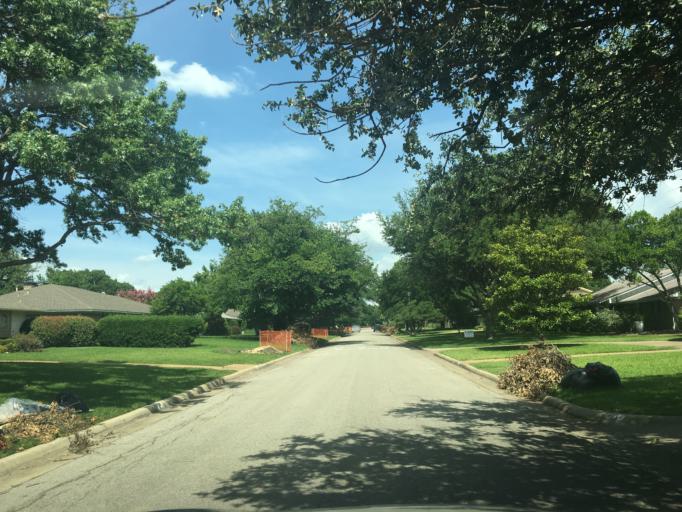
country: US
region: Texas
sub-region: Dallas County
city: Addison
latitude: 32.9122
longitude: -96.8427
